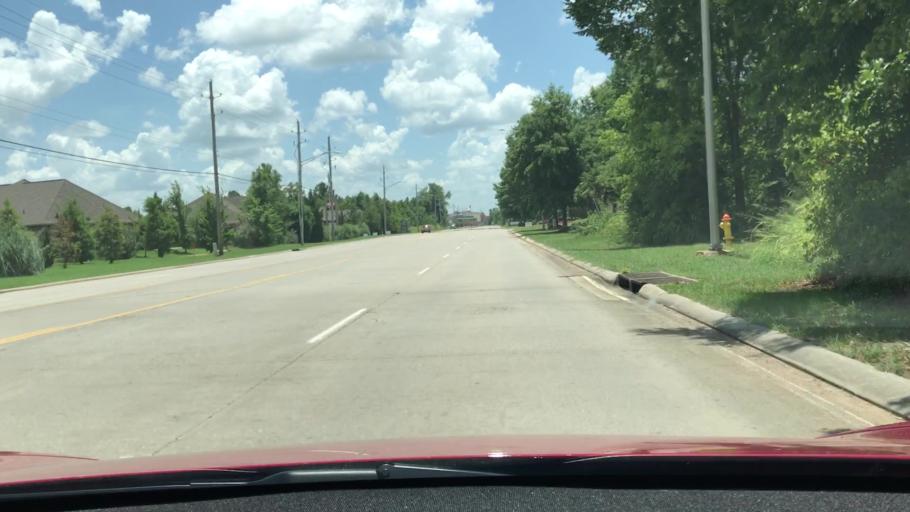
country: US
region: Louisiana
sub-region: Bossier Parish
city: Bossier City
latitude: 32.4328
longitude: -93.7262
